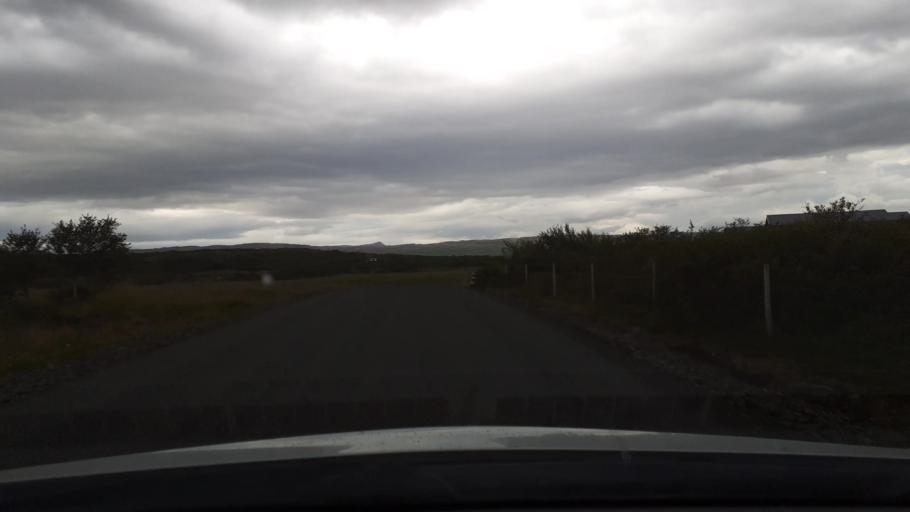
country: IS
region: West
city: Borgarnes
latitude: 64.6759
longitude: -21.7080
